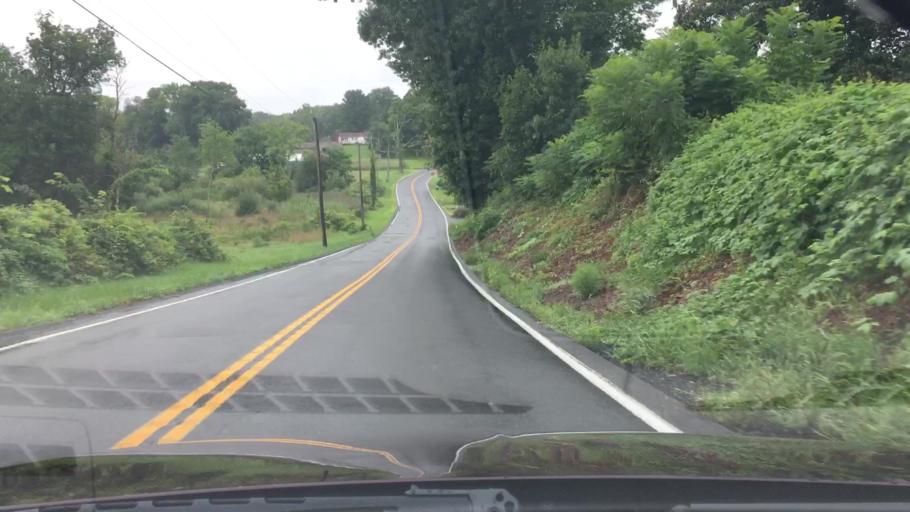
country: US
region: Connecticut
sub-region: Hartford County
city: Tariffville
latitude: 41.9411
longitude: -72.7476
